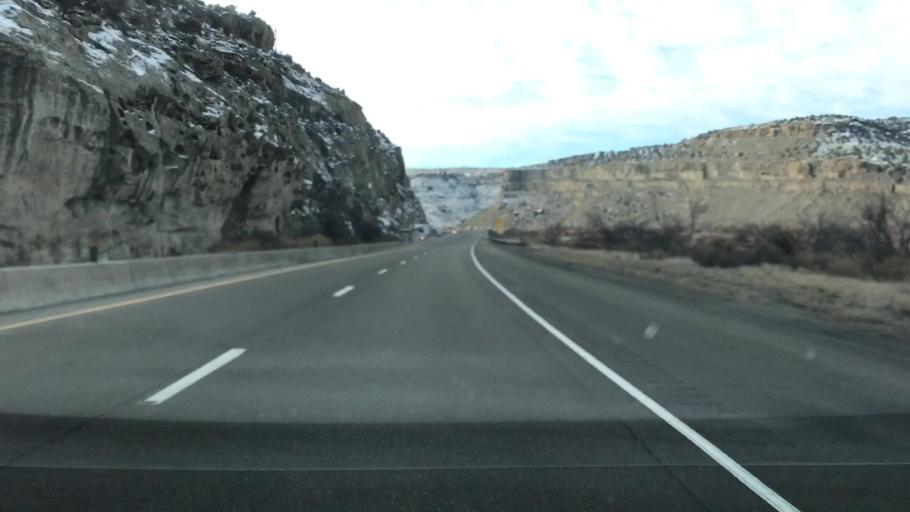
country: US
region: Colorado
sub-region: Mesa County
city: Palisade
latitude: 39.2652
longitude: -108.2549
